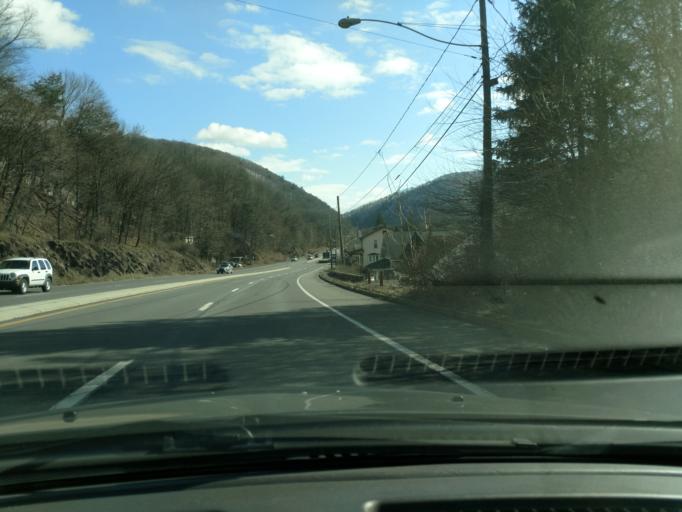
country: US
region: Pennsylvania
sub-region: Berks County
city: West Hamburg
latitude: 40.5866
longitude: -76.0256
